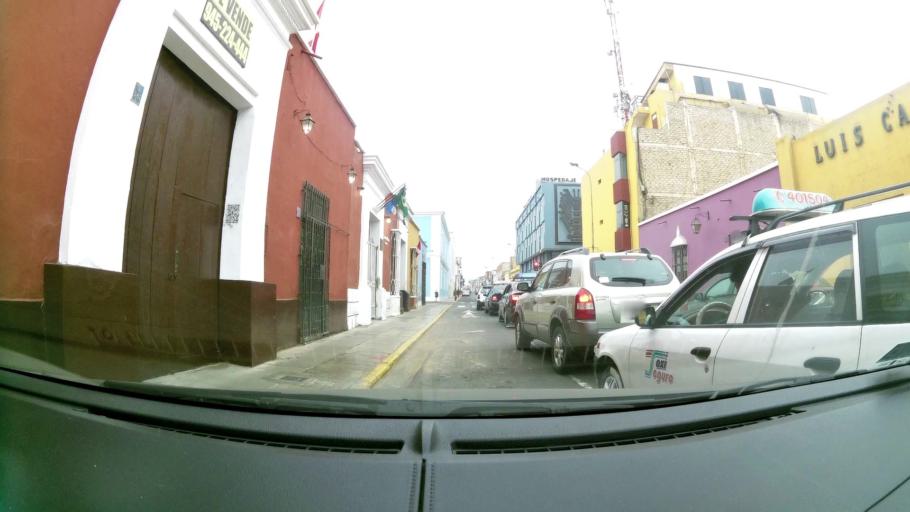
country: PE
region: La Libertad
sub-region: Provincia de Trujillo
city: Trujillo
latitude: -8.1090
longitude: -79.0287
